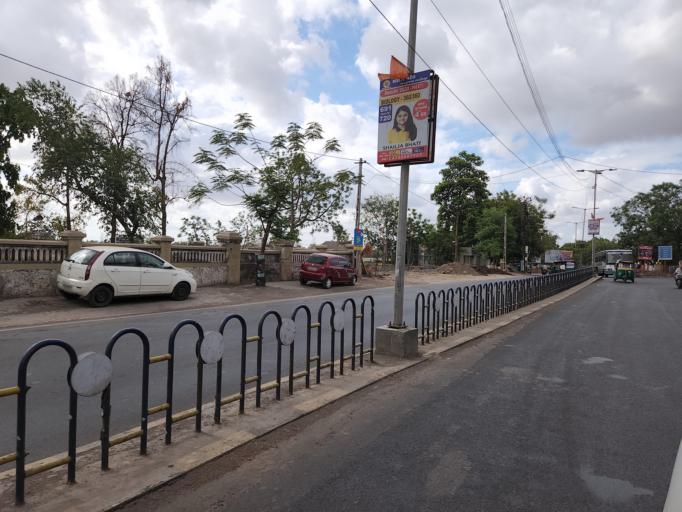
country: IN
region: Gujarat
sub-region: Bhavnagar
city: Bhavnagar
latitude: 21.7658
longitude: 72.1478
